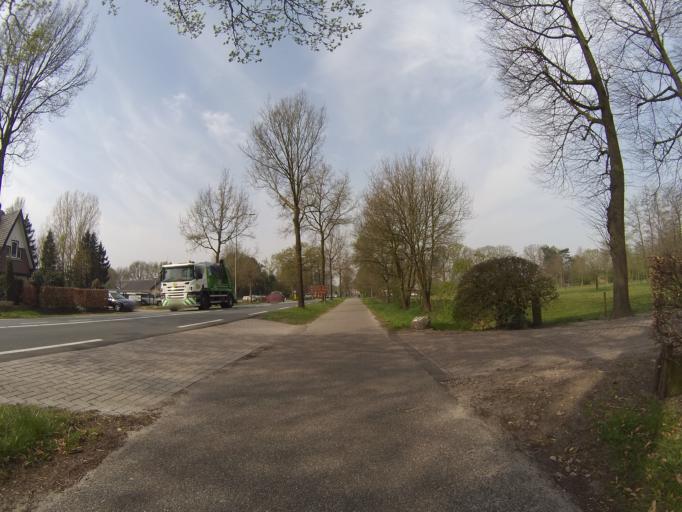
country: NL
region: Utrecht
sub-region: Gemeente Soest
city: Soest
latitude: 52.1607
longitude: 5.3316
